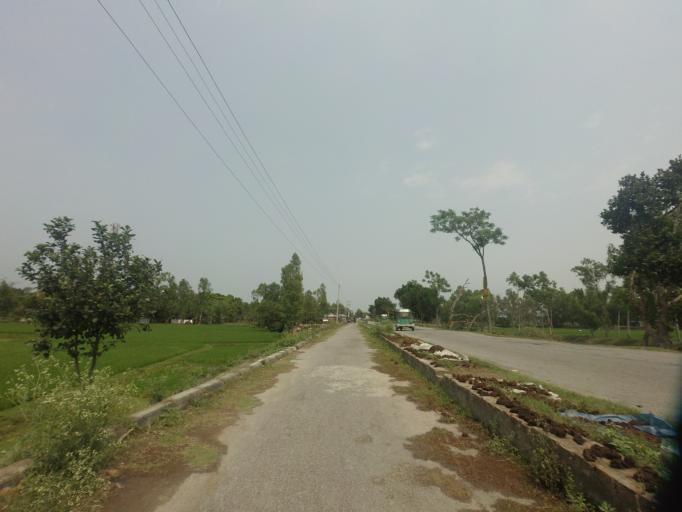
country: BD
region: Rajshahi
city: Sirajganj
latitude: 24.3589
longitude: 89.7055
